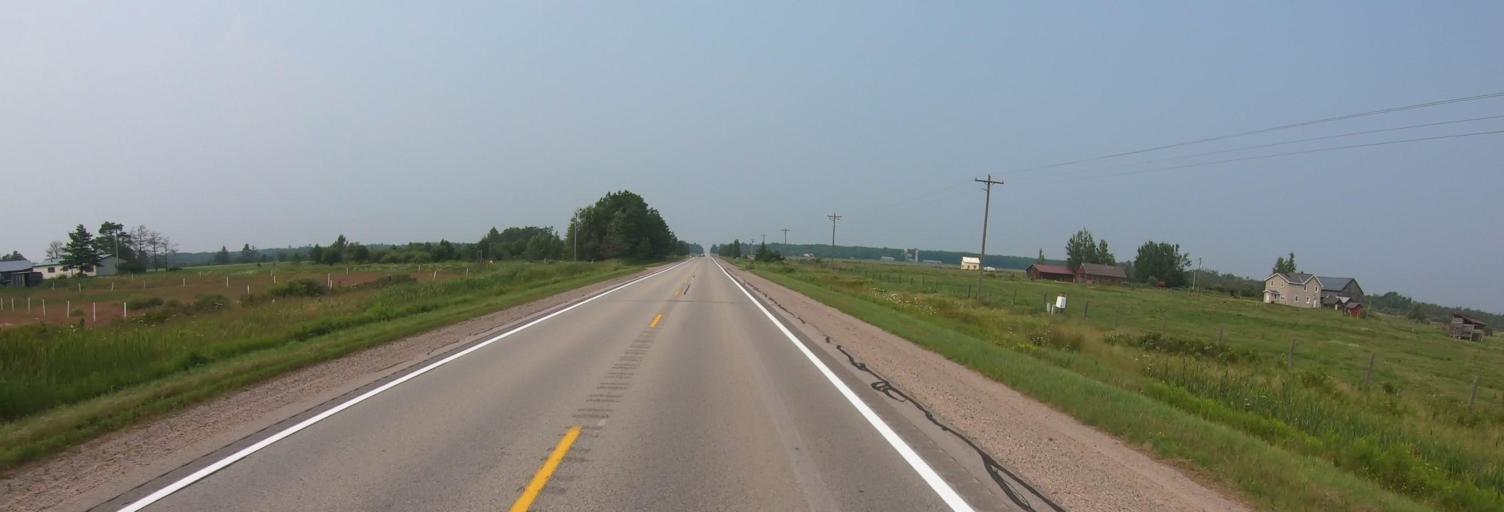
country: US
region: Michigan
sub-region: Chippewa County
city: Sault Ste. Marie
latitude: 46.1942
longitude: -84.3635
